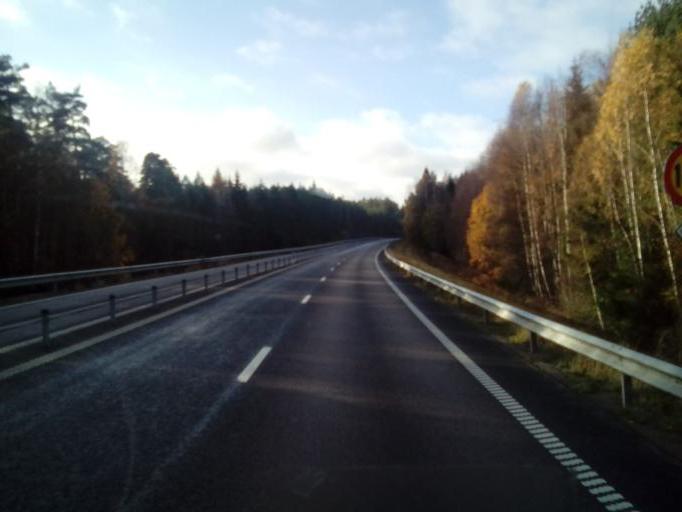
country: SE
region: Kalmar
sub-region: Vimmerby Kommun
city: Vimmerby
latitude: 57.6718
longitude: 15.9308
